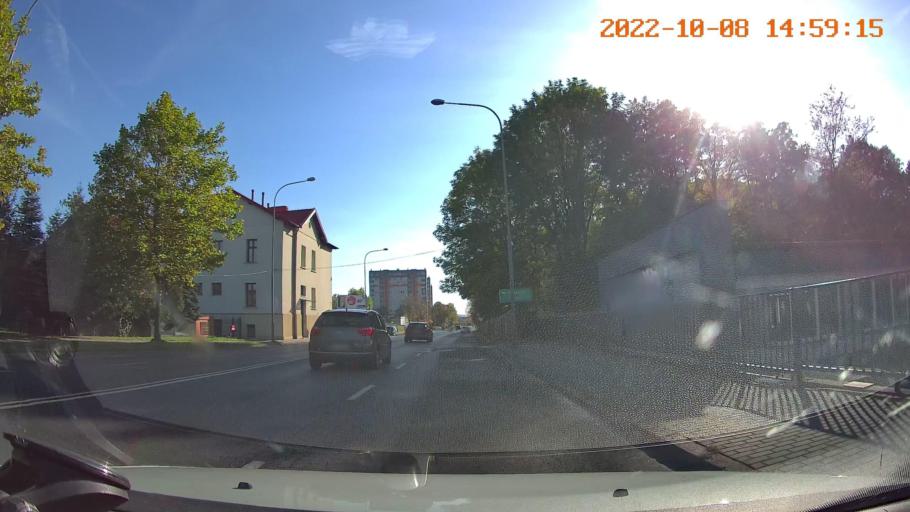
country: PL
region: Lesser Poland Voivodeship
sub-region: Powiat tarnowski
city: Tarnow
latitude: 50.0200
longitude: 20.9968
